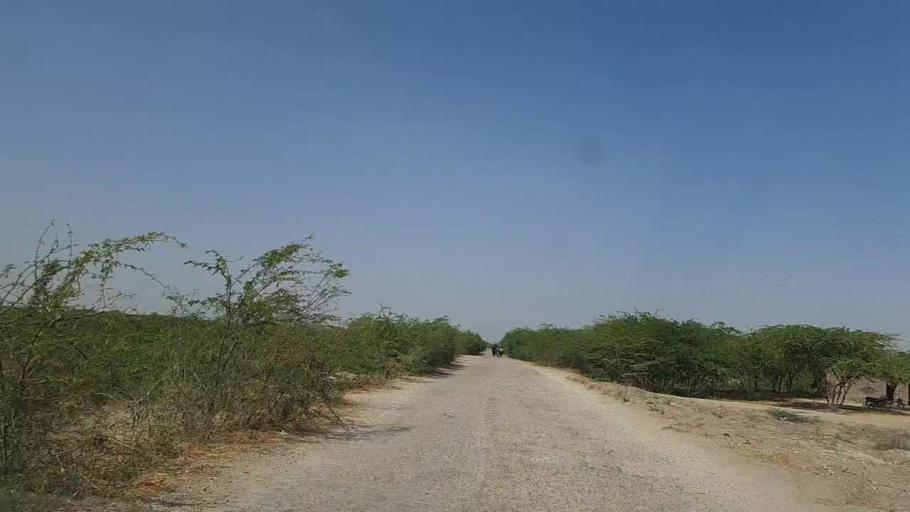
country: PK
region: Sindh
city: Naukot
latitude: 24.6467
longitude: 69.2879
